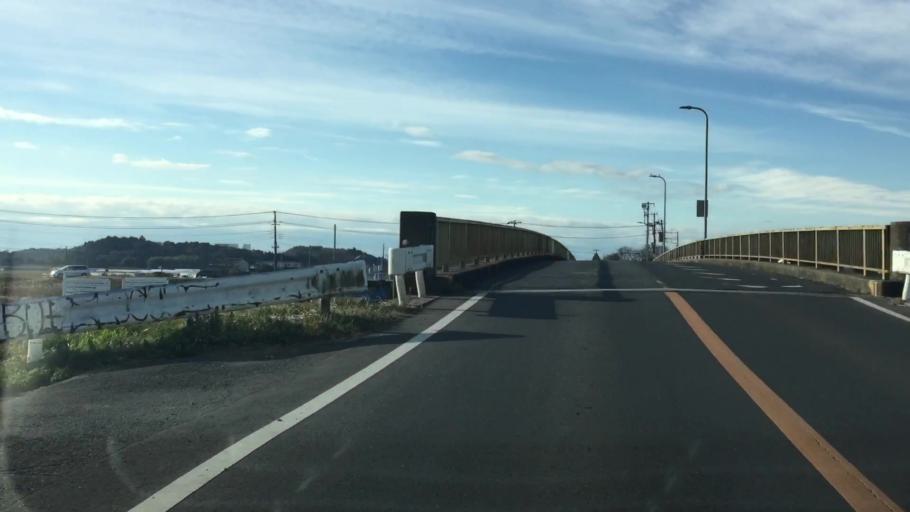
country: JP
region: Ibaraki
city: Toride
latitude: 35.8412
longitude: 140.1306
